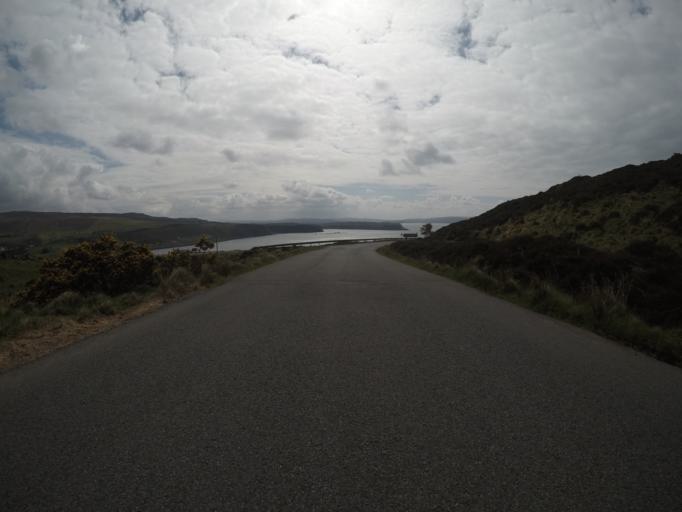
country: GB
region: Scotland
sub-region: Highland
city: Portree
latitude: 57.5937
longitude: -6.3734
